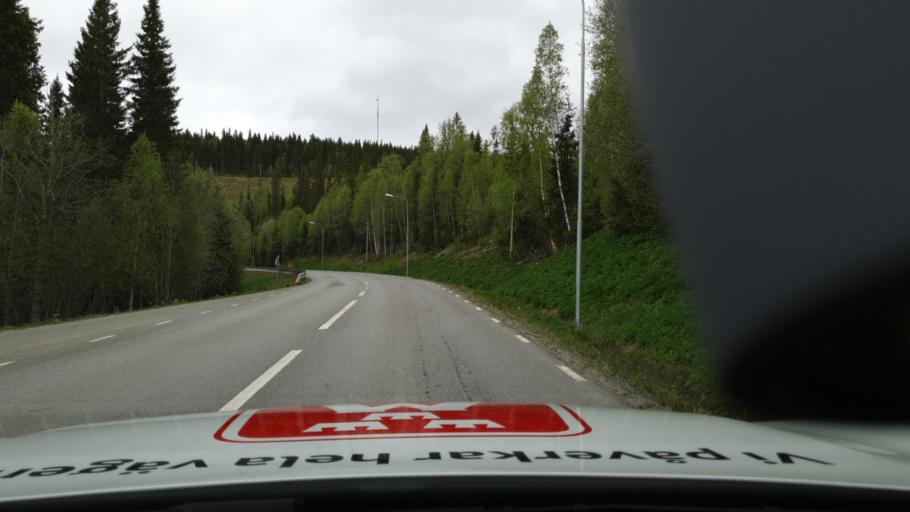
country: NO
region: Nord-Trondelag
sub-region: Lierne
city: Sandvika
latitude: 64.4922
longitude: 14.1372
